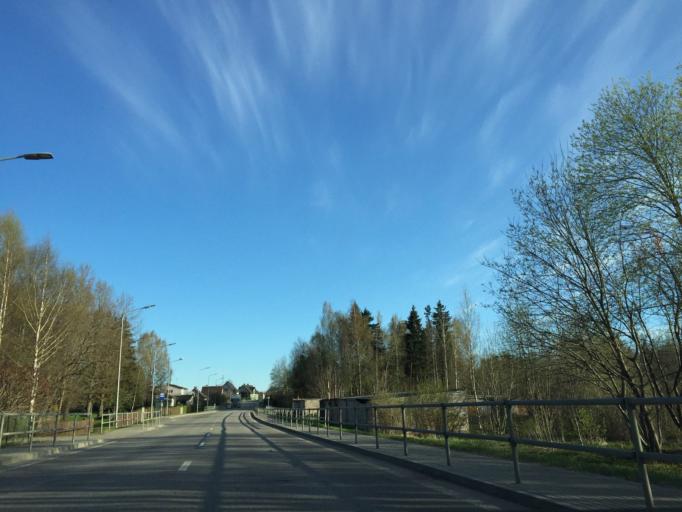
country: LV
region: Valkas Rajons
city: Valka
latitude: 57.7786
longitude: 25.9925
